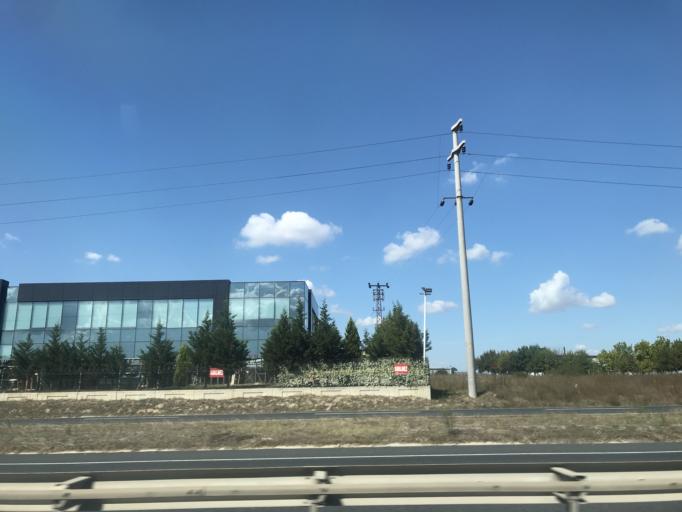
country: TR
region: Tekirdag
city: Corlu
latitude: 41.2001
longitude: 27.8319
